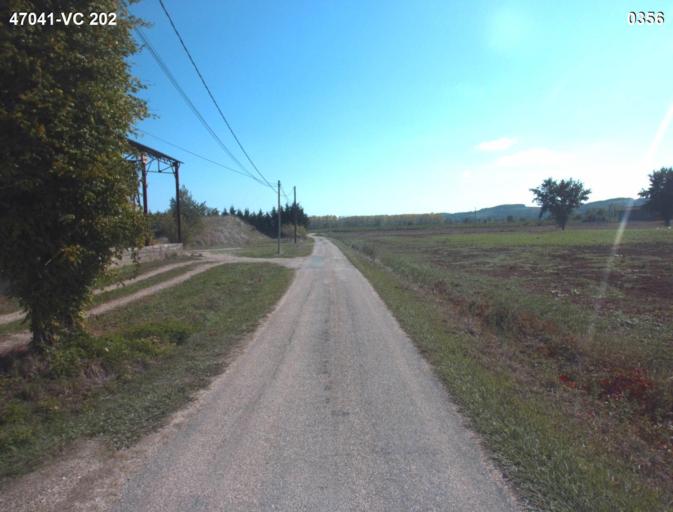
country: FR
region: Aquitaine
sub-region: Departement du Lot-et-Garonne
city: Port-Sainte-Marie
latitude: 44.2170
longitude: 0.3968
